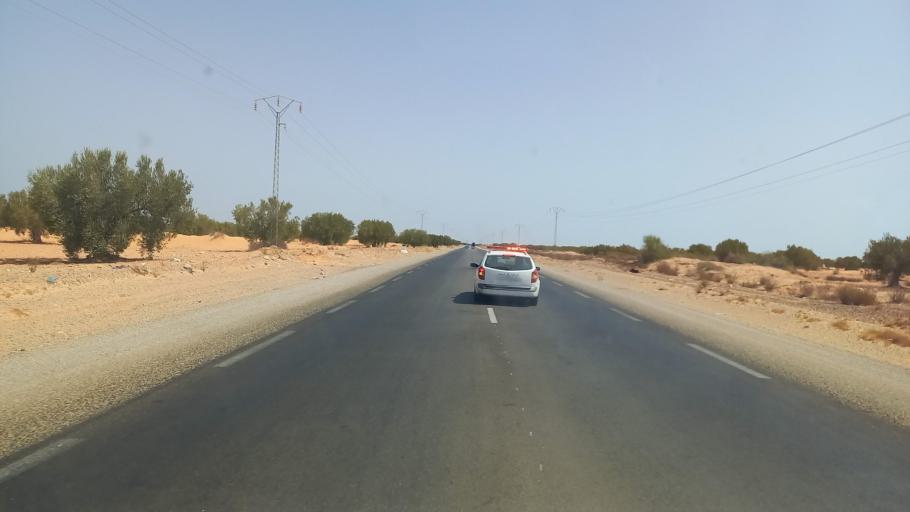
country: TN
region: Madanin
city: Zarzis
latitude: 33.4173
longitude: 10.8738
